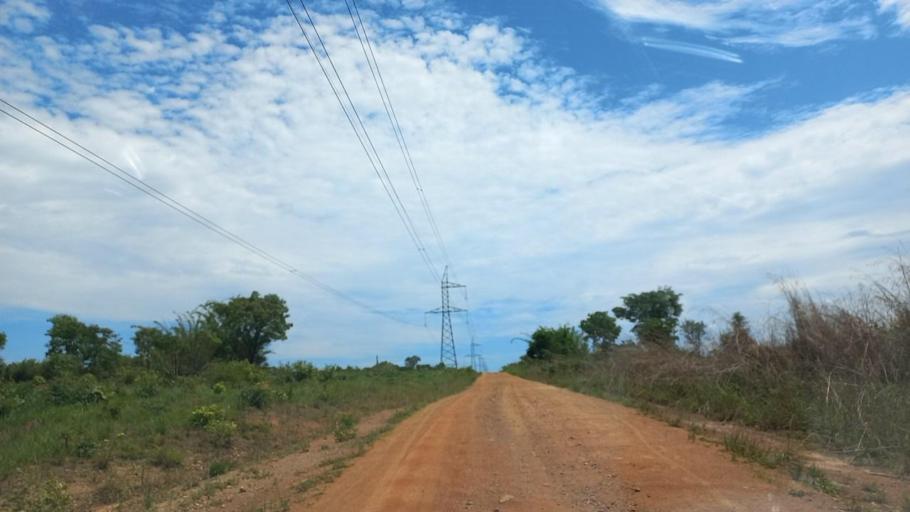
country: ZM
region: Copperbelt
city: Kitwe
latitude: -12.8130
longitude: 28.3583
